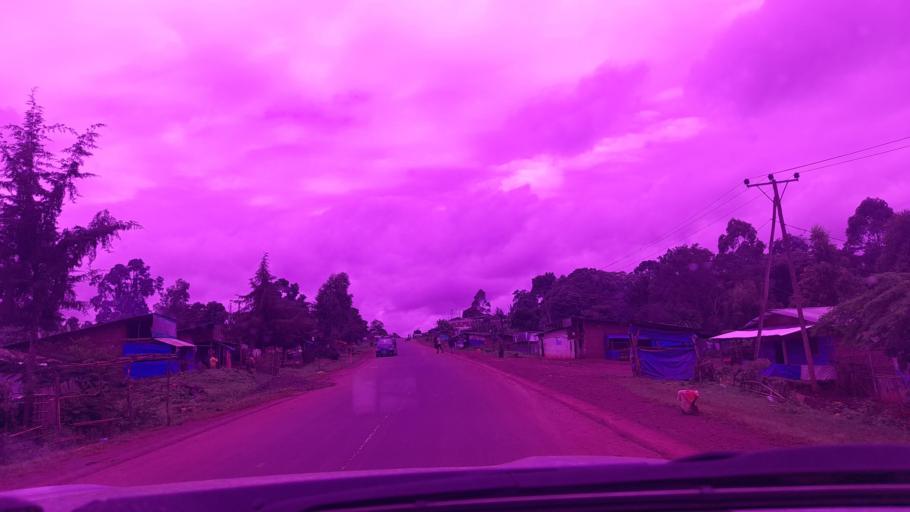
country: ET
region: Southern Nations, Nationalities, and People's Region
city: Bonga
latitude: 7.2985
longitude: 35.9892
